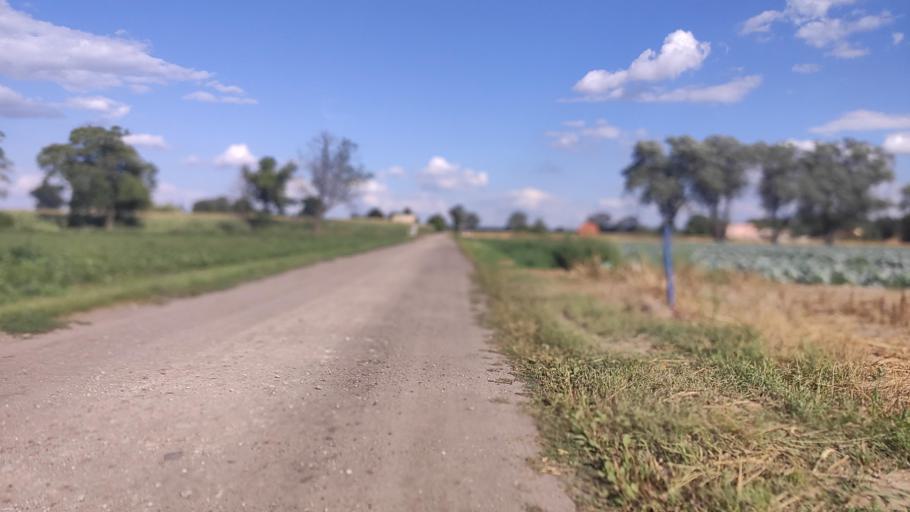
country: PL
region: Greater Poland Voivodeship
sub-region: Powiat poznanski
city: Swarzedz
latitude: 52.4108
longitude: 17.1354
